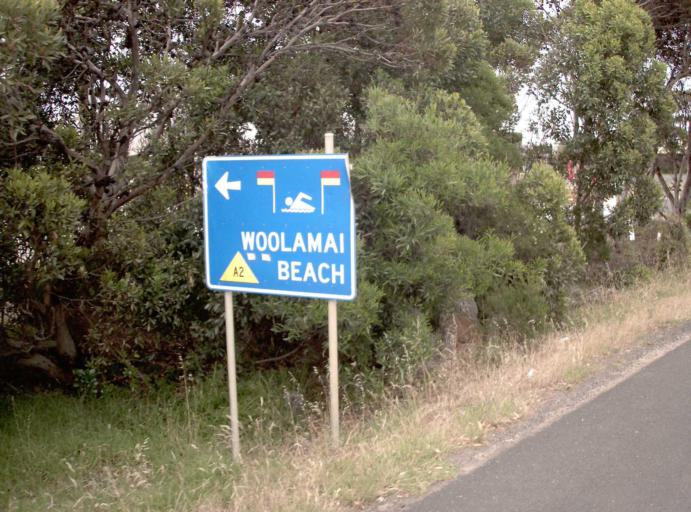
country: AU
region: Victoria
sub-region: Bass Coast
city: Phillip Island
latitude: -38.5209
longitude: 145.3359
